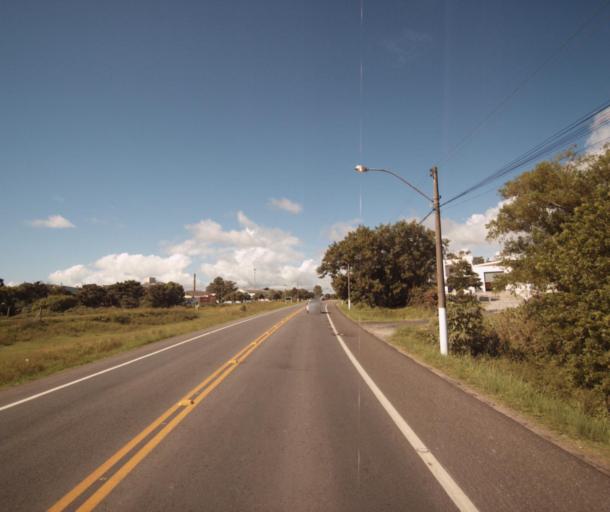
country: BR
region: Rio Grande do Sul
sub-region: Pelotas
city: Pelotas
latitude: -31.7616
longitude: -52.3562
